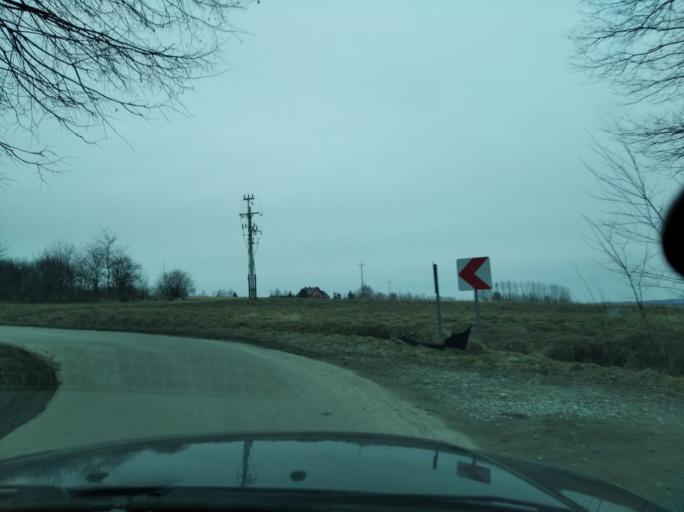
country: PL
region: Subcarpathian Voivodeship
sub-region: Powiat rzeszowski
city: Chmielnik
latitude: 49.9817
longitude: 22.1520
